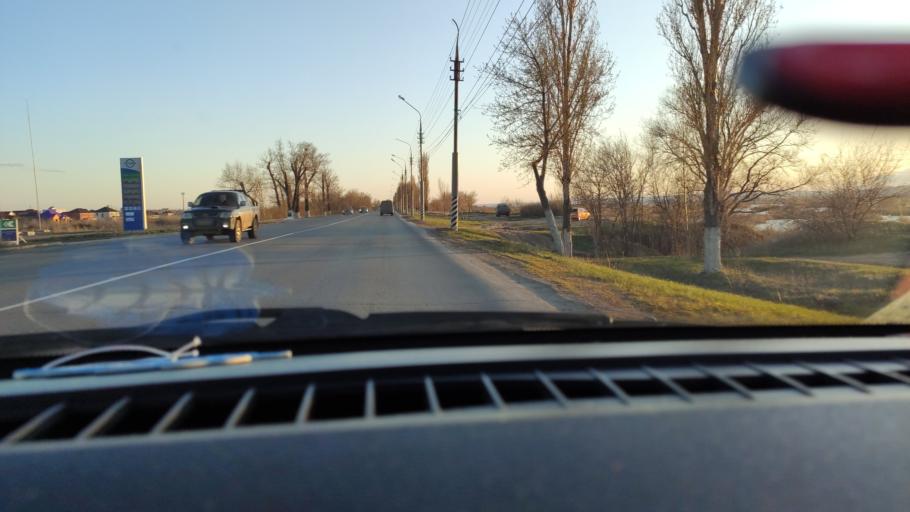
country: RU
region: Saratov
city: Privolzhskiy
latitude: 51.4387
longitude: 46.0647
